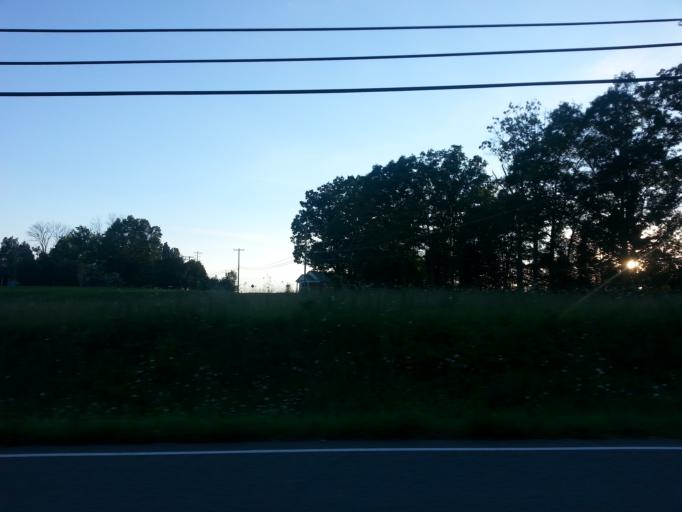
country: US
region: Tennessee
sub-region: Loudon County
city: Lenoir City
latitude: 35.8557
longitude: -84.2256
